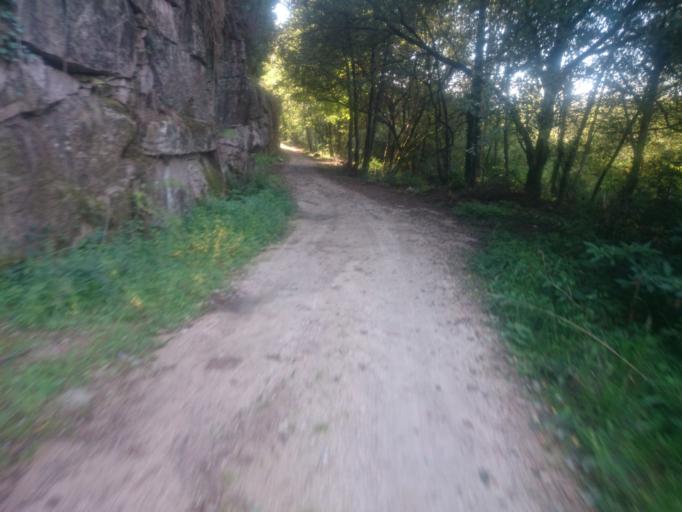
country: ES
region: Galicia
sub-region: Provincia de Pontevedra
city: Porrino
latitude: 42.1564
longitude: -8.6097
